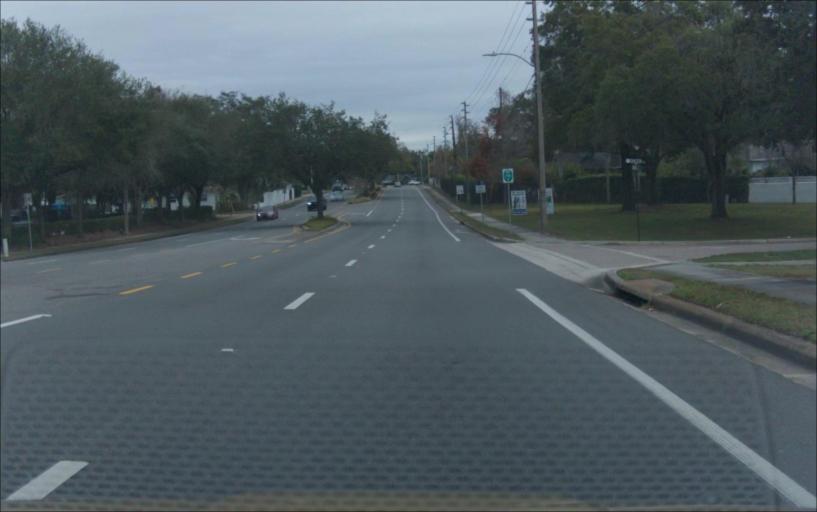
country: US
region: Florida
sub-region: Orange County
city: Maitland
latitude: 28.6253
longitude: -81.3381
